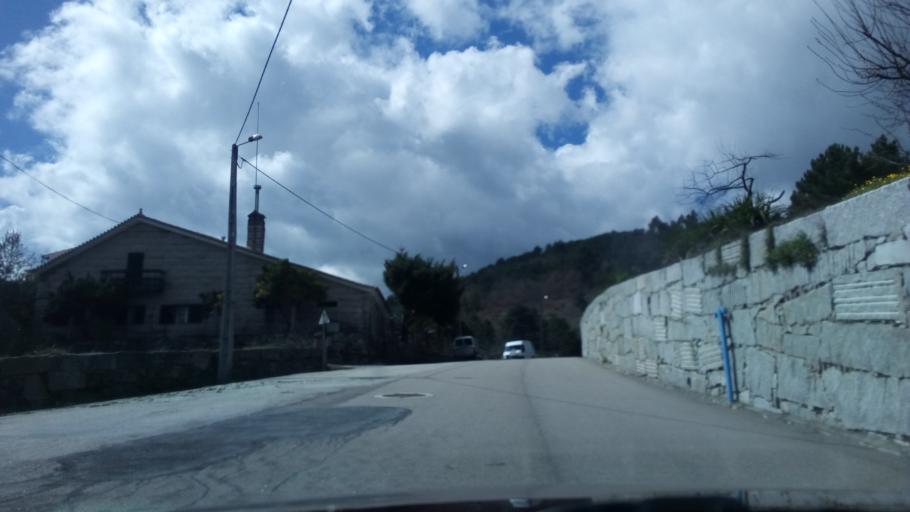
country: PT
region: Guarda
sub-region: Fornos de Algodres
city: Fornos de Algodres
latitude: 40.6620
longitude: -7.4965
